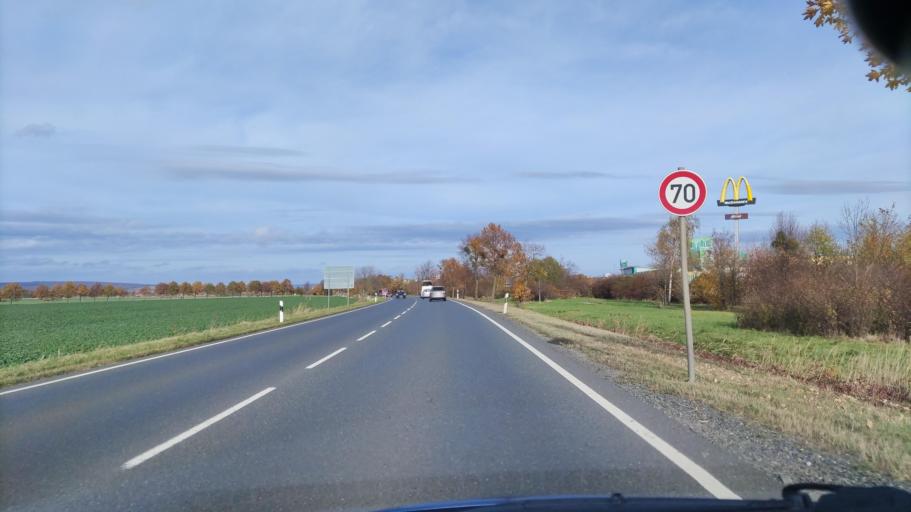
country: DE
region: Lower Saxony
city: Goslar
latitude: 51.9271
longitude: 10.4100
